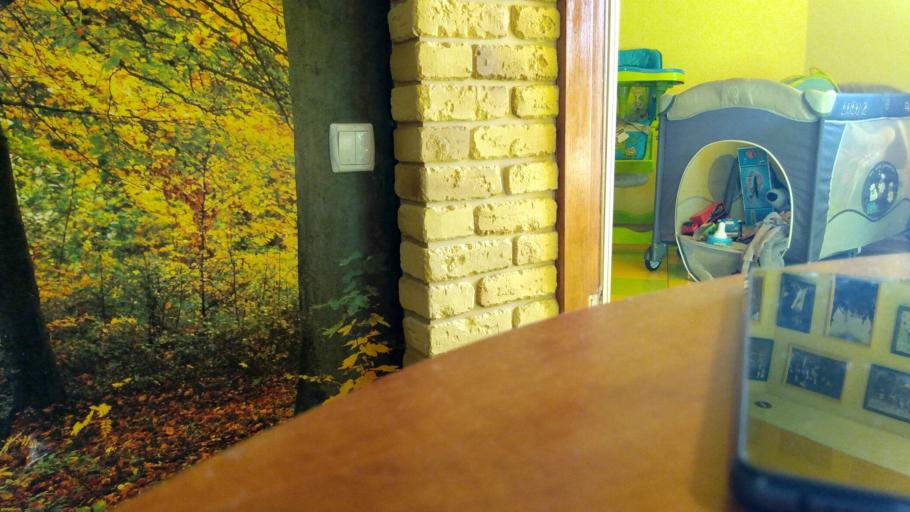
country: RU
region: Tverskaya
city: Likhoslavl'
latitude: 57.1769
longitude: 35.5603
